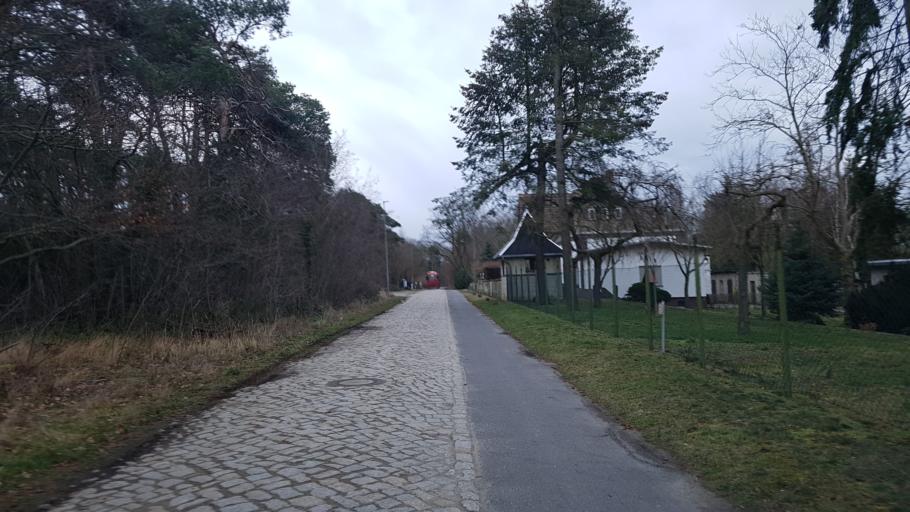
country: DE
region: Brandenburg
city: Plessa
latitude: 51.4740
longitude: 13.5791
